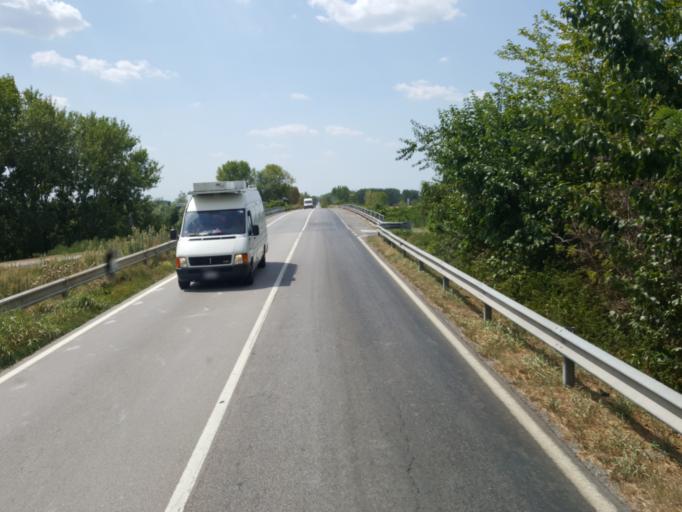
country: IT
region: Lombardy
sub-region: Provincia di Mantova
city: Roncoferraro
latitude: 45.0913
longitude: 10.9497
